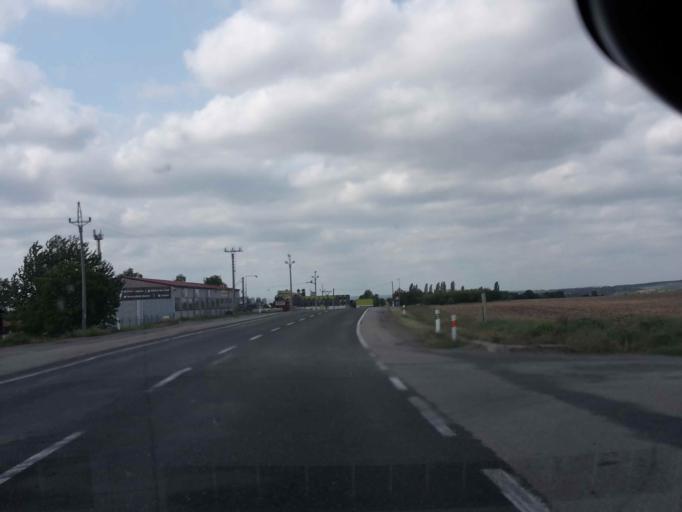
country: CZ
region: South Moravian
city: Vinicne Sumice
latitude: 49.1842
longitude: 16.8136
